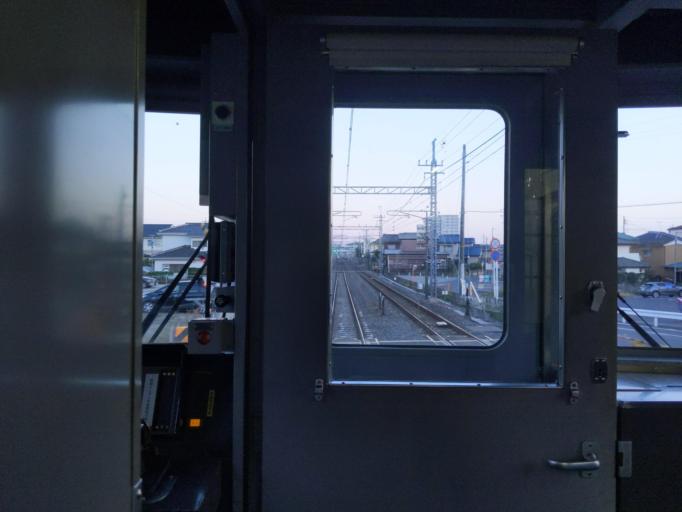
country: JP
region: Chiba
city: Noda
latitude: 35.9346
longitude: 139.8879
